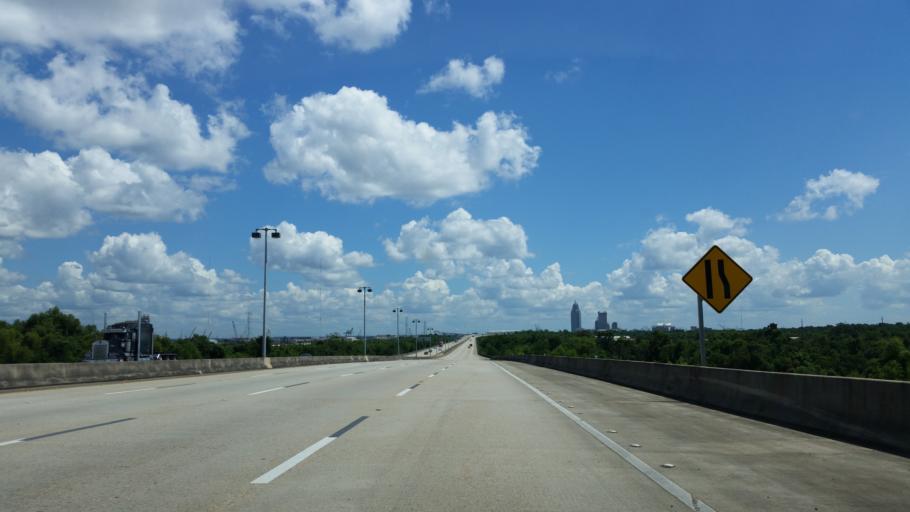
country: US
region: Alabama
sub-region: Mobile County
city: Prichard
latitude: 30.7230
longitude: -88.0673
